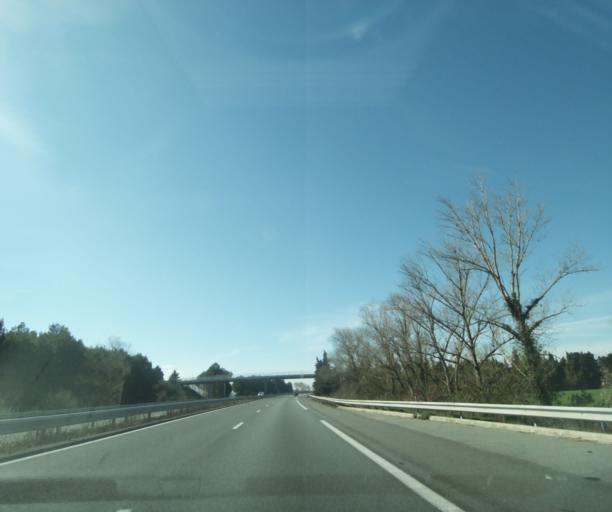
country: FR
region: Languedoc-Roussillon
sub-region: Departement de l'Aude
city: Lavalette
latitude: 43.2036
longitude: 2.2533
